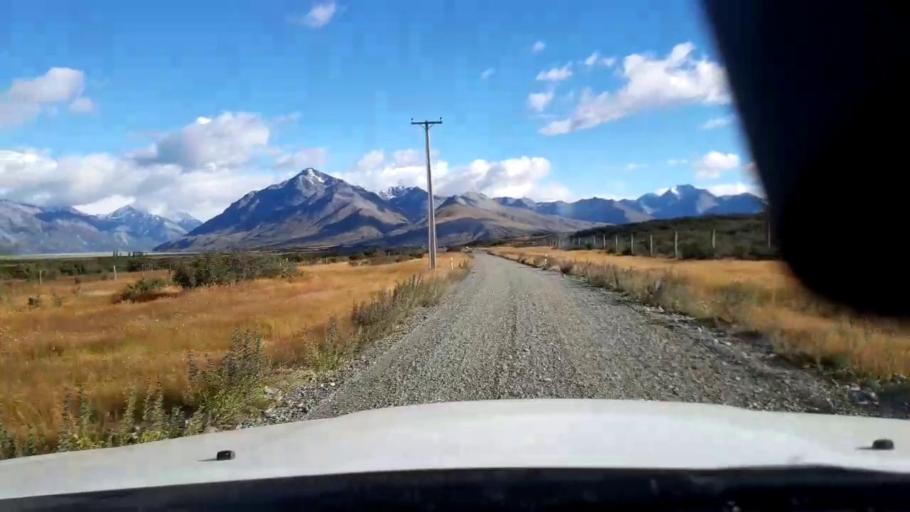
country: NZ
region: Canterbury
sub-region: Timaru District
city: Pleasant Point
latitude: -43.7657
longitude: 170.5698
